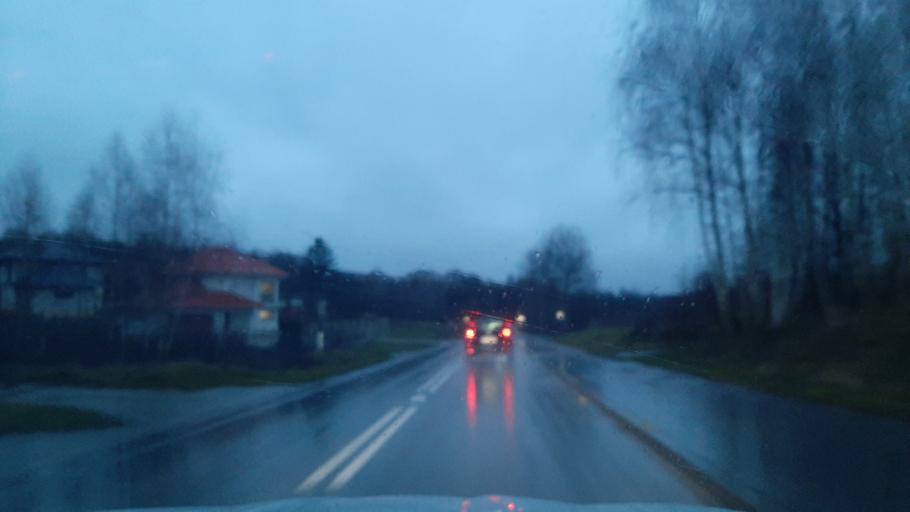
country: PL
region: Lublin Voivodeship
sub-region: Powiat lubelski
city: Lublin
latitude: 51.3214
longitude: 22.5283
